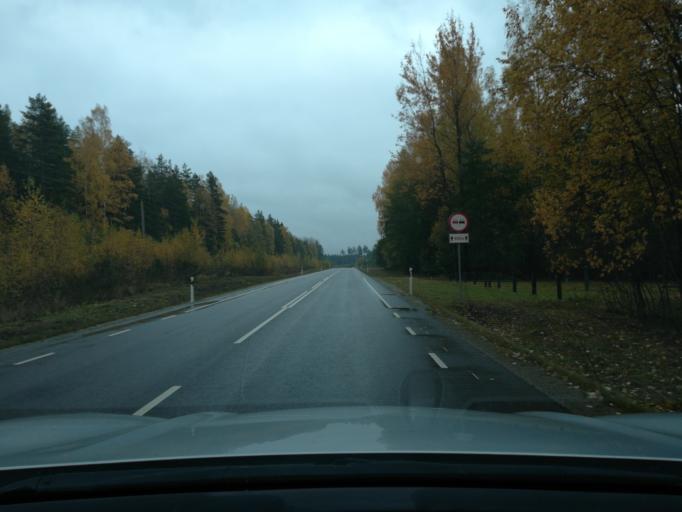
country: EE
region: Ida-Virumaa
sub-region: Johvi vald
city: Johvi
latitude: 59.3045
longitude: 27.4641
